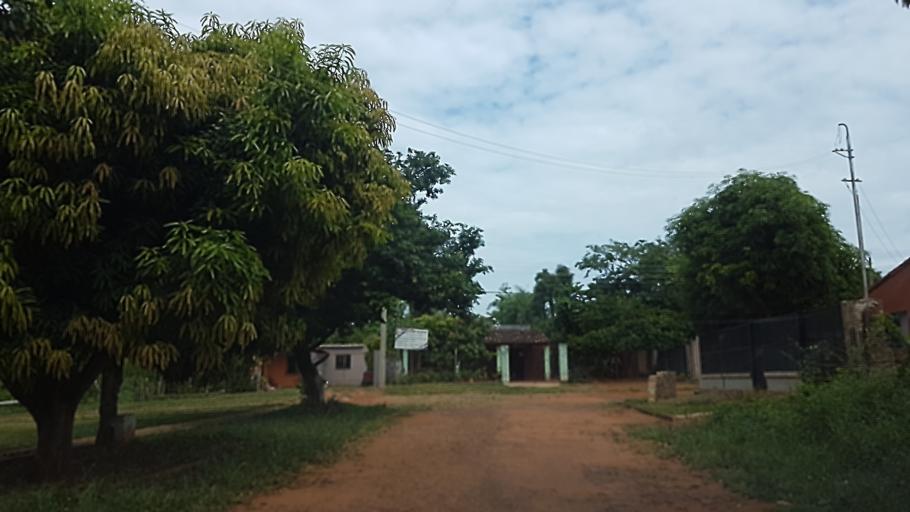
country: PY
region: Central
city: Capiata
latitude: -25.3792
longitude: -57.4621
